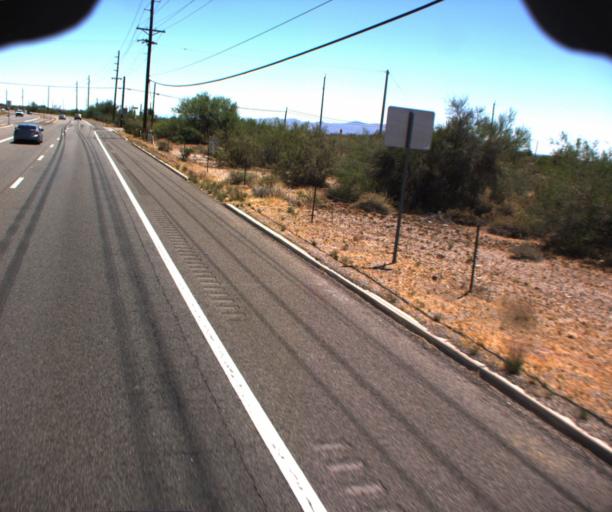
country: US
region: Arizona
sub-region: Maricopa County
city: Wickenburg
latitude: 33.8553
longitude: -112.6242
